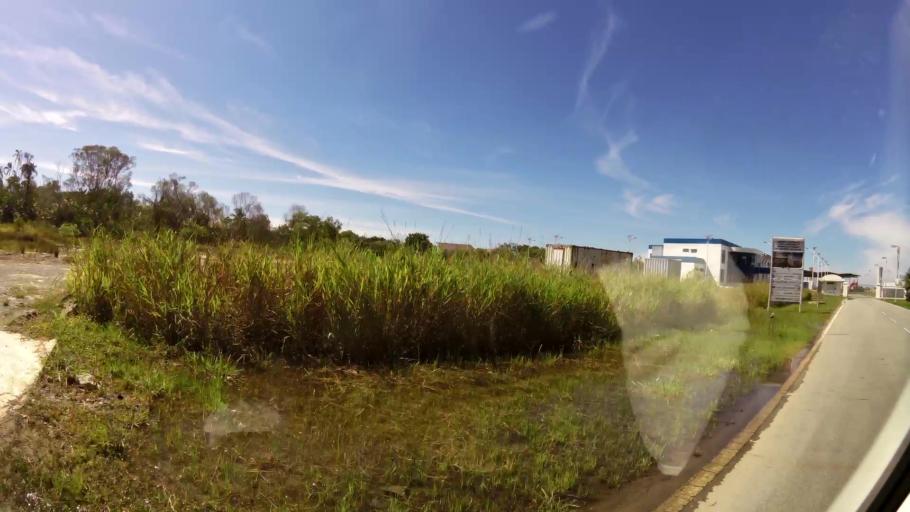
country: BN
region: Brunei and Muara
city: Bandar Seri Begawan
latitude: 5.0031
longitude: 115.0638
